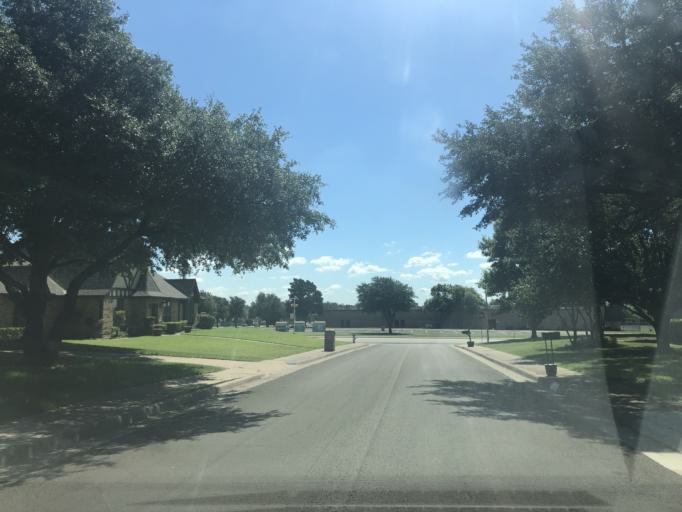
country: US
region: Texas
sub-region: Dallas County
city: Duncanville
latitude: 32.6466
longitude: -96.9347
